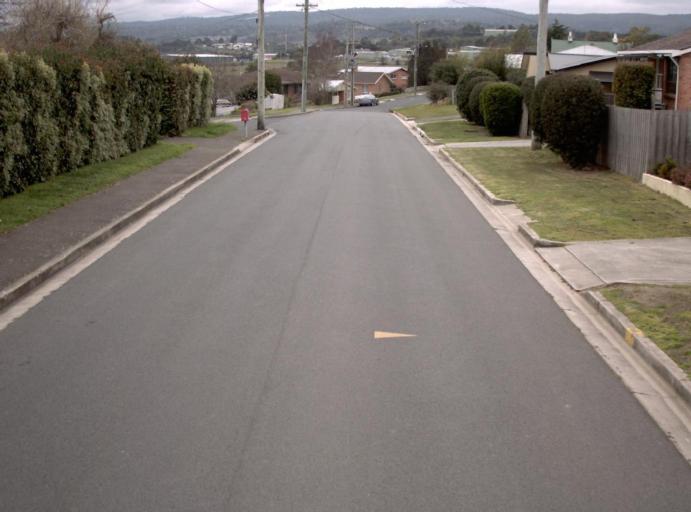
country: AU
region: Tasmania
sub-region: Launceston
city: Newstead
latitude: -41.4489
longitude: 147.1777
